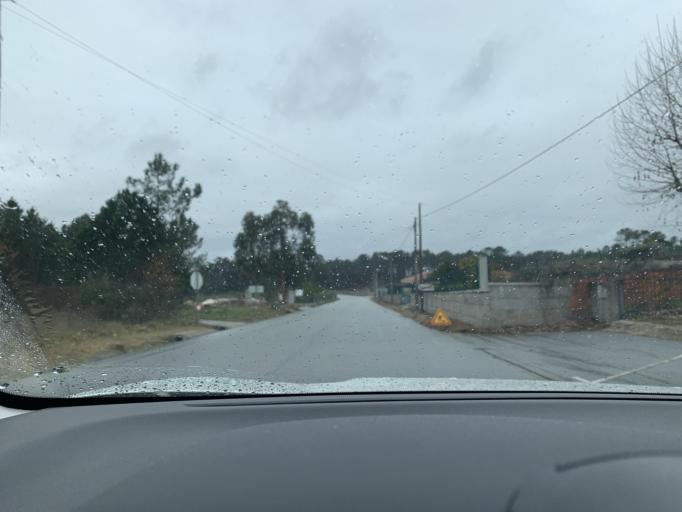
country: PT
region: Viseu
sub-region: Mangualde
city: Mangualde
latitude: 40.5974
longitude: -7.8191
